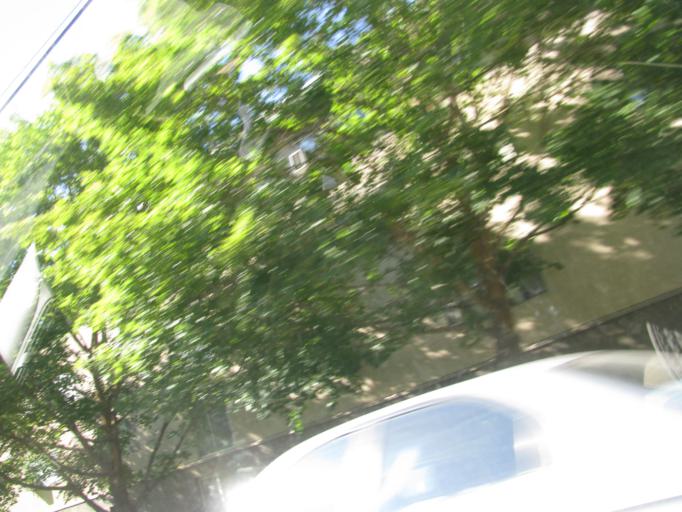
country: US
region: Washington
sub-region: Spokane County
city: Spokane
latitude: 47.6574
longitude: -117.4444
